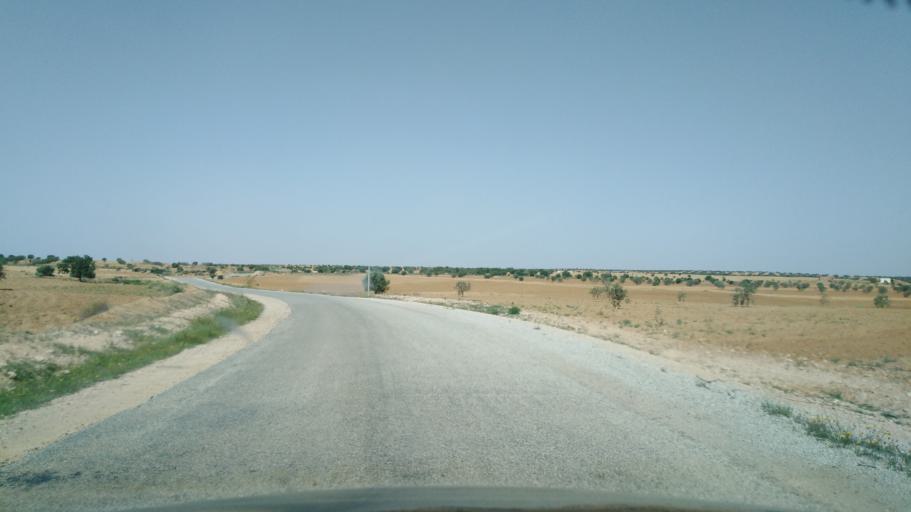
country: TN
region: Safaqis
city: Bi'r `Ali Bin Khalifah
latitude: 34.6784
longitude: 10.4157
